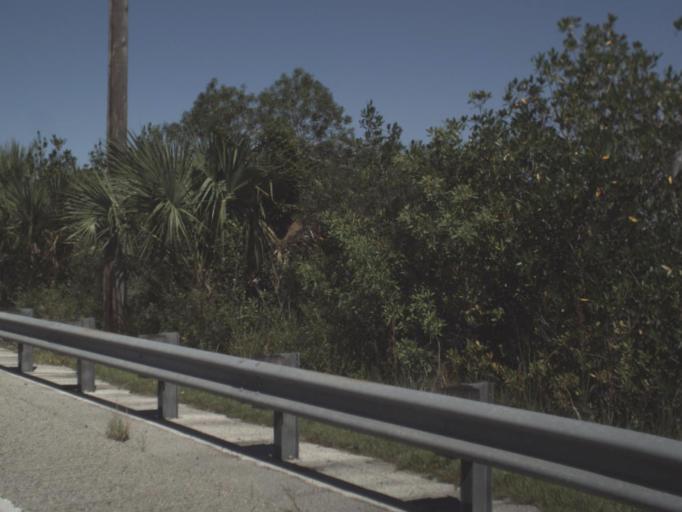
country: US
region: Florida
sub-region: Collier County
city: Marco
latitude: 25.9580
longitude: -81.4910
